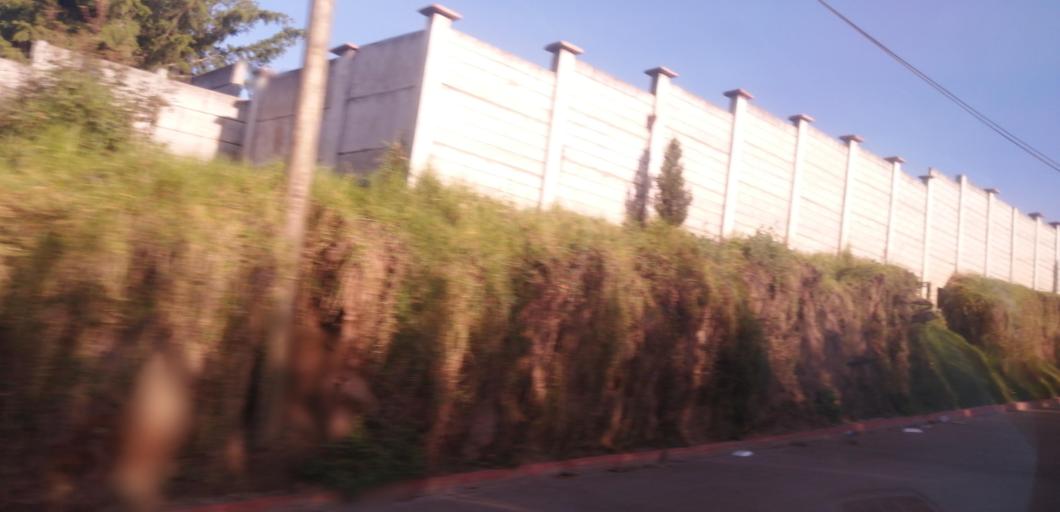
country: GT
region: Quetzaltenango
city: Olintepeque
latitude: 14.8680
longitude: -91.5391
